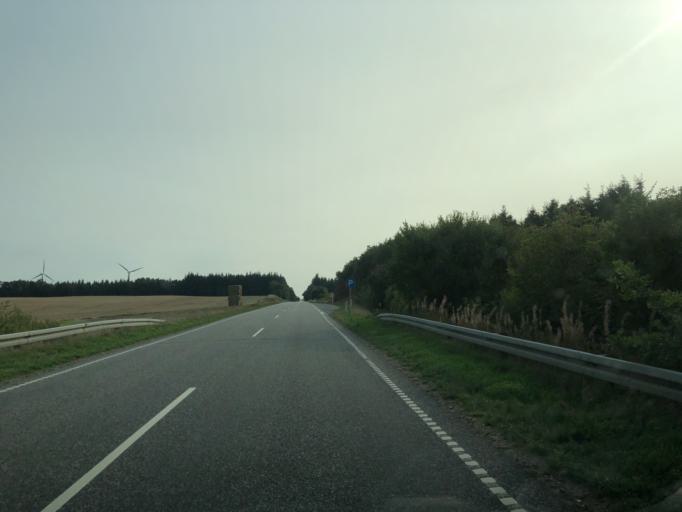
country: DK
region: Central Jutland
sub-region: Herning Kommune
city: Vildbjerg
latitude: 56.1803
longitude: 8.6986
